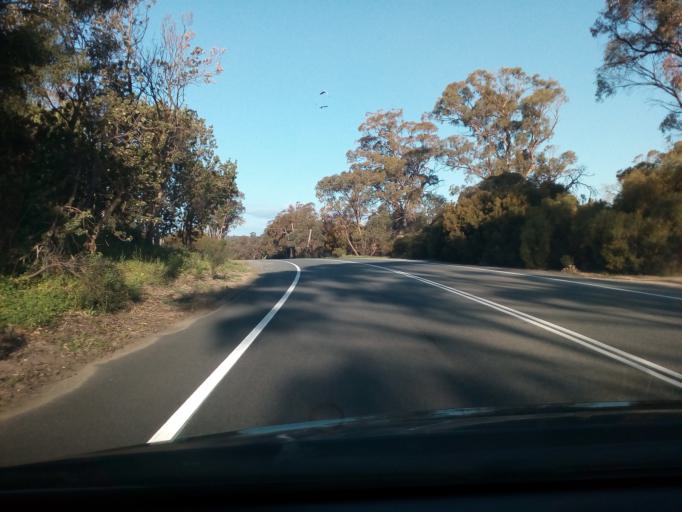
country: AU
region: Western Australia
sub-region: Kwinana
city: Medina
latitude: -32.2503
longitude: 115.7931
